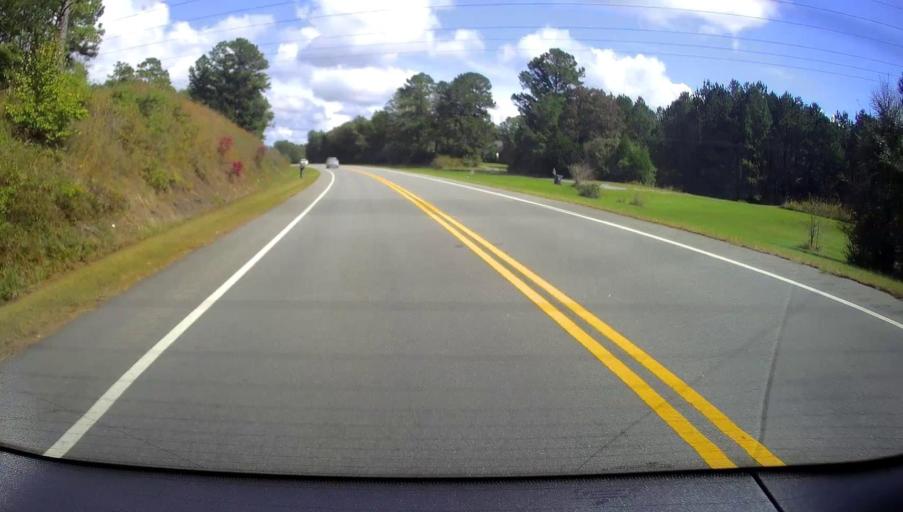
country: US
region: Georgia
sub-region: Baldwin County
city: Milledgeville
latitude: 33.0732
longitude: -83.3208
